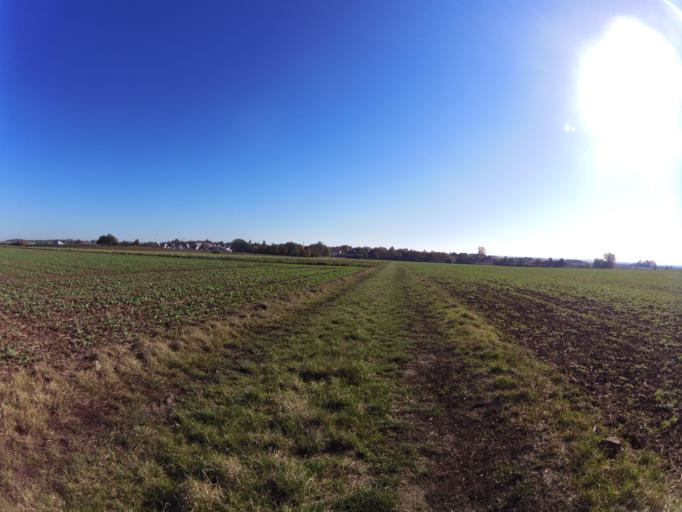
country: DE
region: Bavaria
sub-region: Regierungsbezirk Unterfranken
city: Giebelstadt
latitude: 49.6611
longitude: 9.9337
